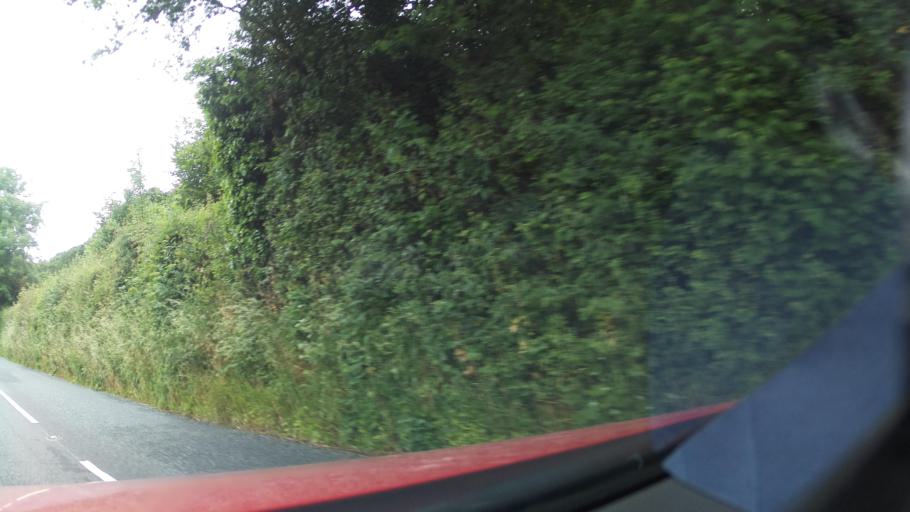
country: GB
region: England
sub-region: Devon
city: Chudleigh
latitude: 50.6802
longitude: -3.6500
